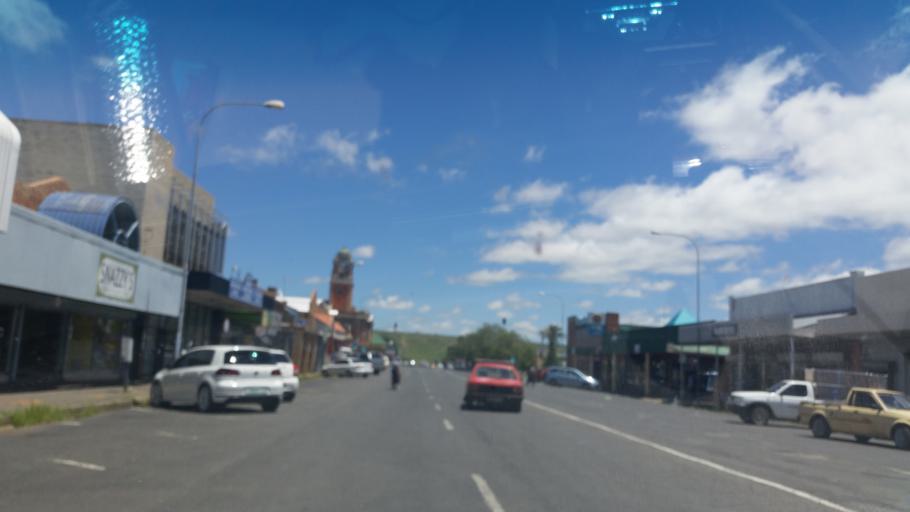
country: ZA
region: Orange Free State
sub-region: Thabo Mofutsanyana District Municipality
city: Harrismith
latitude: -28.2713
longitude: 29.1261
